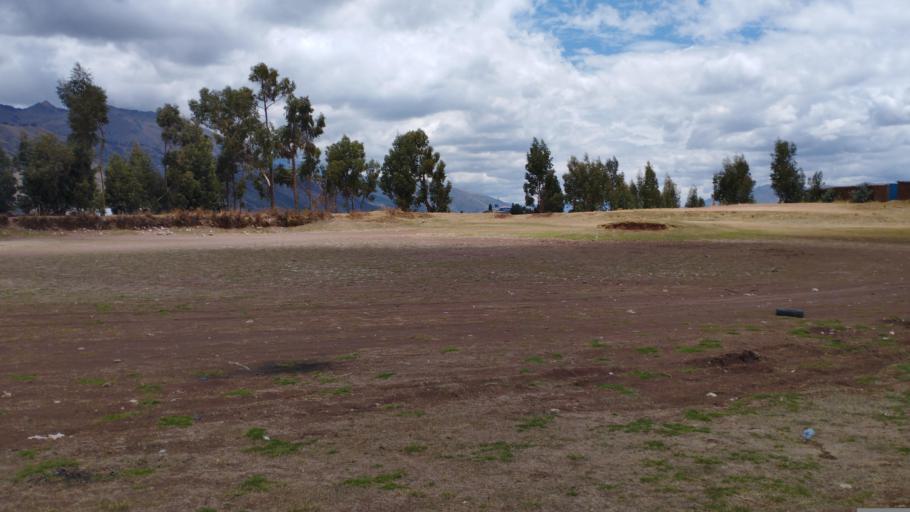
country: PE
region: Cusco
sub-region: Provincia de Cusco
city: Cusco
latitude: -13.5109
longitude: -71.9414
